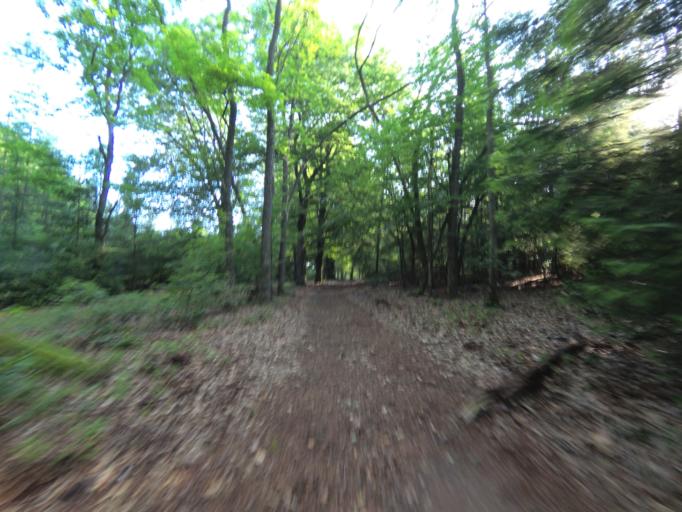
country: NL
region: Gelderland
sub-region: Gemeente Apeldoorn
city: Beekbergen
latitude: 52.1327
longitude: 5.8706
